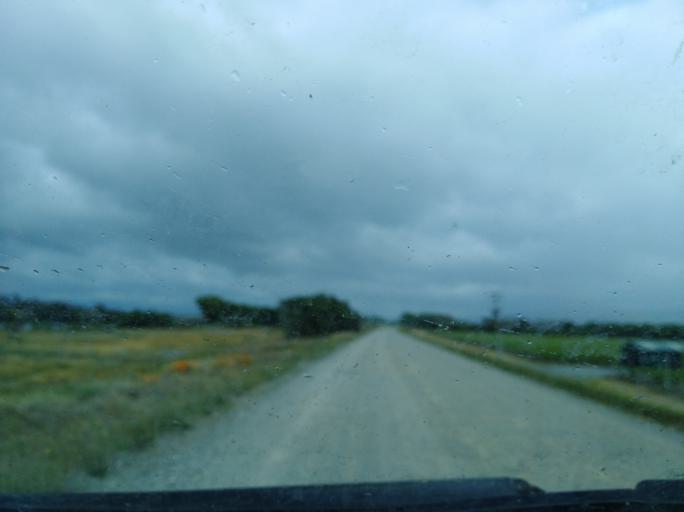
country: NZ
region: Marlborough
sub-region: Marlborough District
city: Blenheim
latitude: -41.4405
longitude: 174.0105
